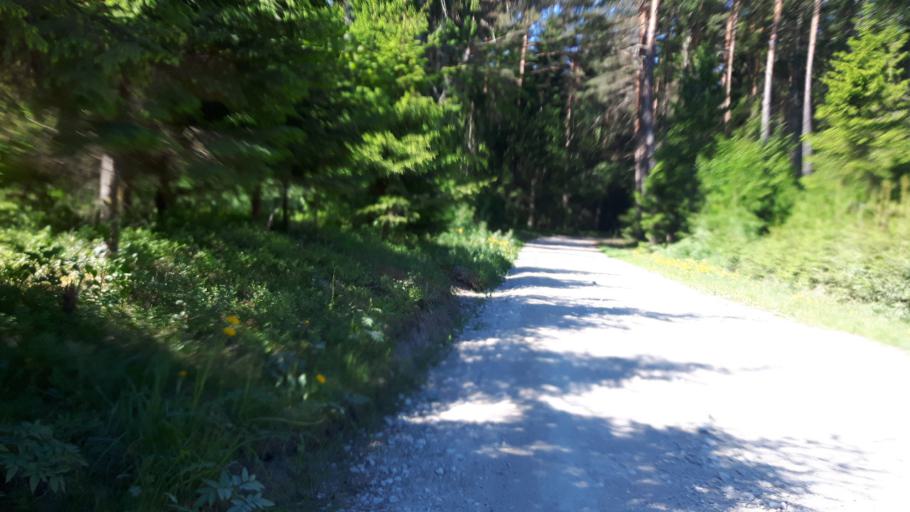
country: EE
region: Harju
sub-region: Loksa linn
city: Loksa
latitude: 59.5587
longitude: 25.8075
